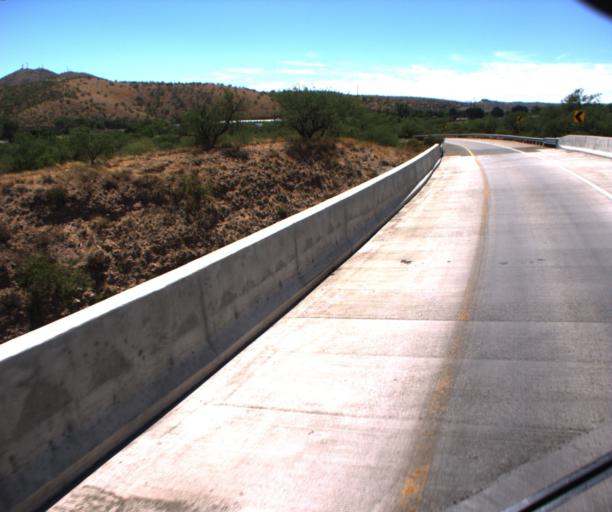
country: US
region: Arizona
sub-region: Santa Cruz County
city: Nogales
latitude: 31.3956
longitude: -110.9600
